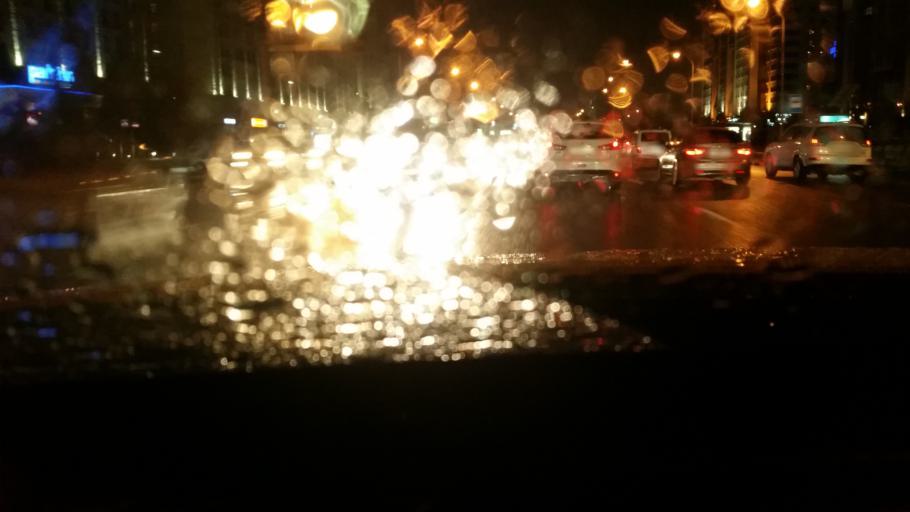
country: KZ
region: Astana Qalasy
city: Astana
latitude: 51.1626
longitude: 71.4099
